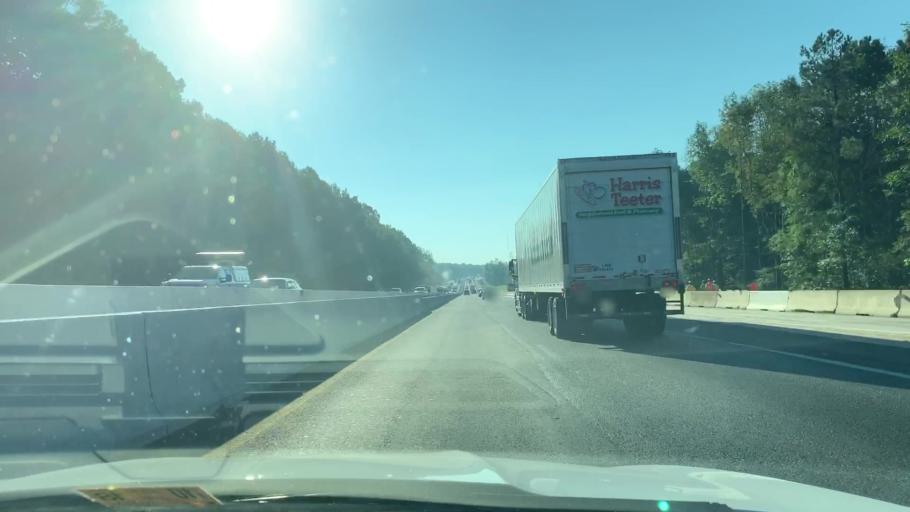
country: US
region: Virginia
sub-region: York County
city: Yorktown
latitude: 37.2114
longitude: -76.5850
